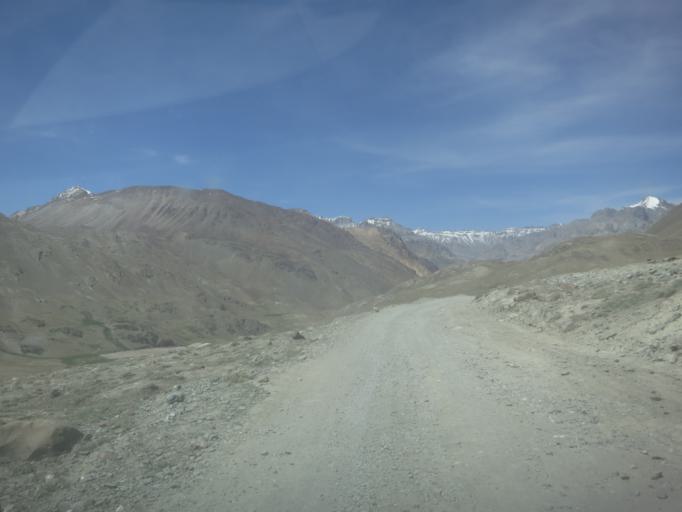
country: IN
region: Himachal Pradesh
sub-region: Kulu
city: Manali
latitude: 32.4001
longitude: 77.6375
